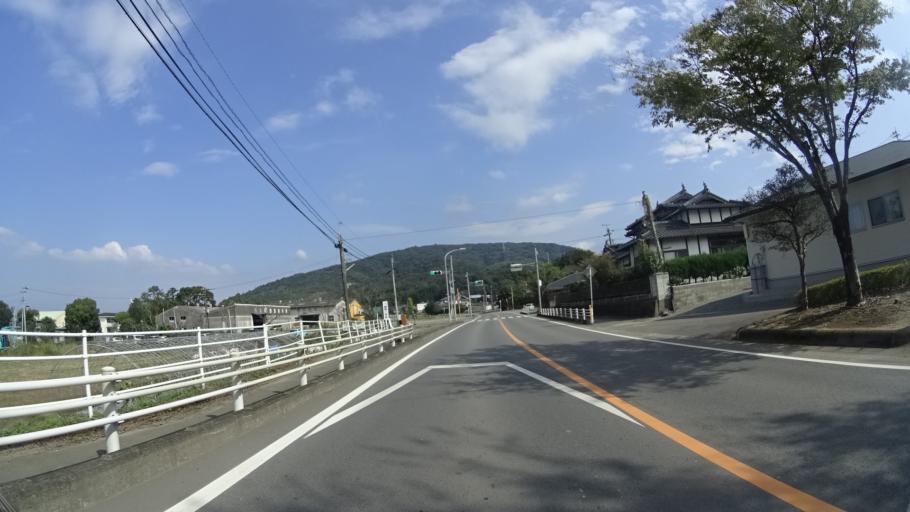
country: JP
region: Kumamoto
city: Ozu
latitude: 32.7577
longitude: 130.8103
